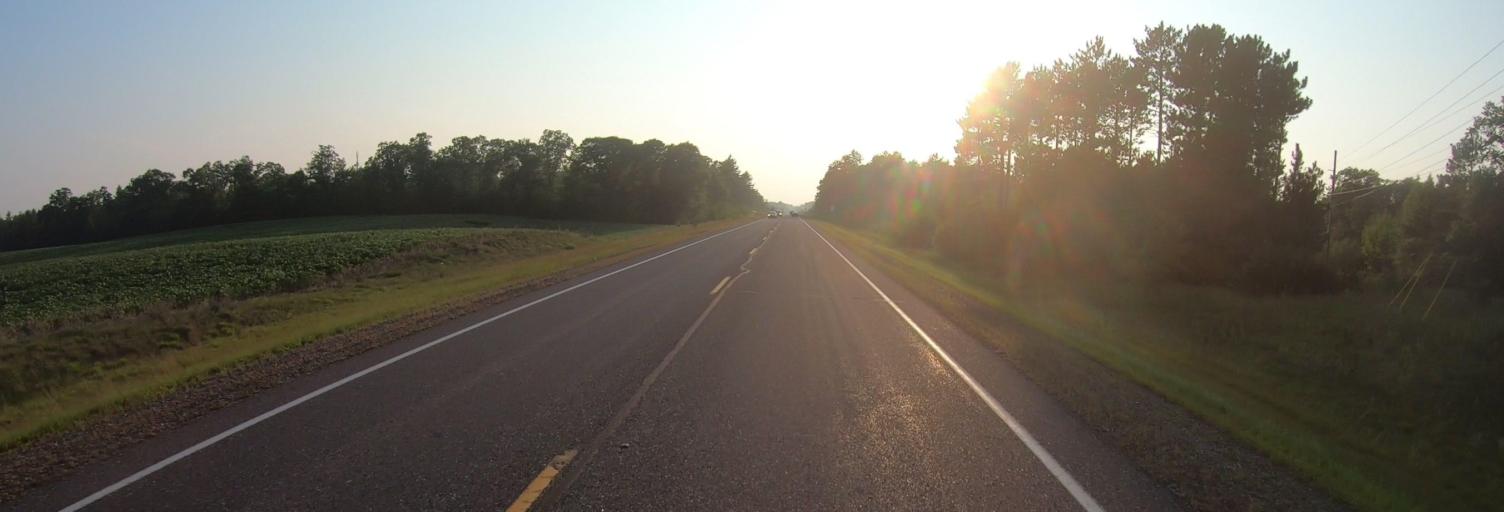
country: US
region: Wisconsin
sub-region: Washburn County
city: Shell Lake
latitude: 45.8156
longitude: -92.0877
